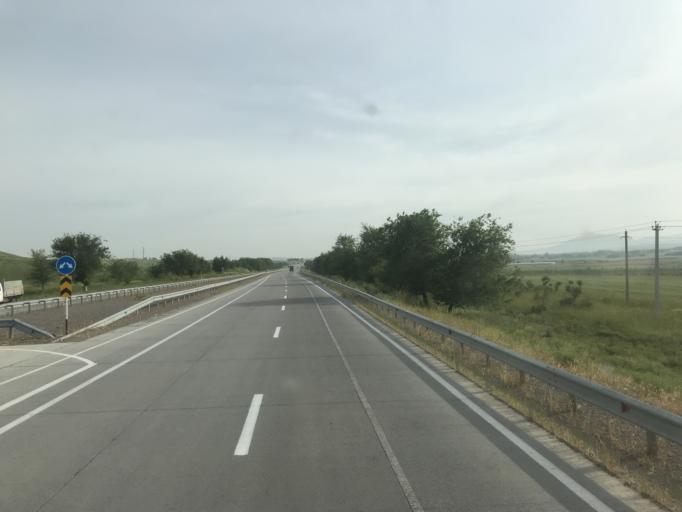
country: KZ
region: Ongtustik Qazaqstan
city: Qazyqurt
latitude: 41.8450
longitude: 69.4065
